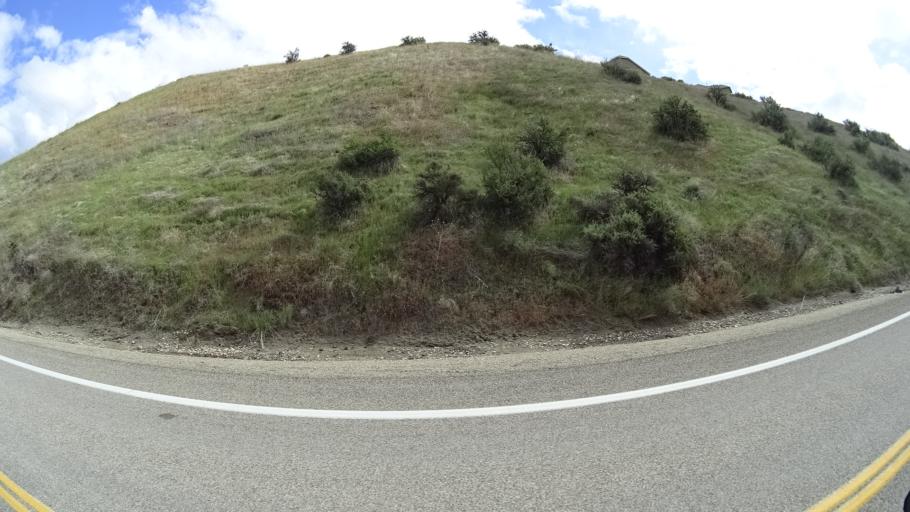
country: US
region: Idaho
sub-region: Ada County
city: Garden City
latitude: 43.7012
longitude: -116.2318
